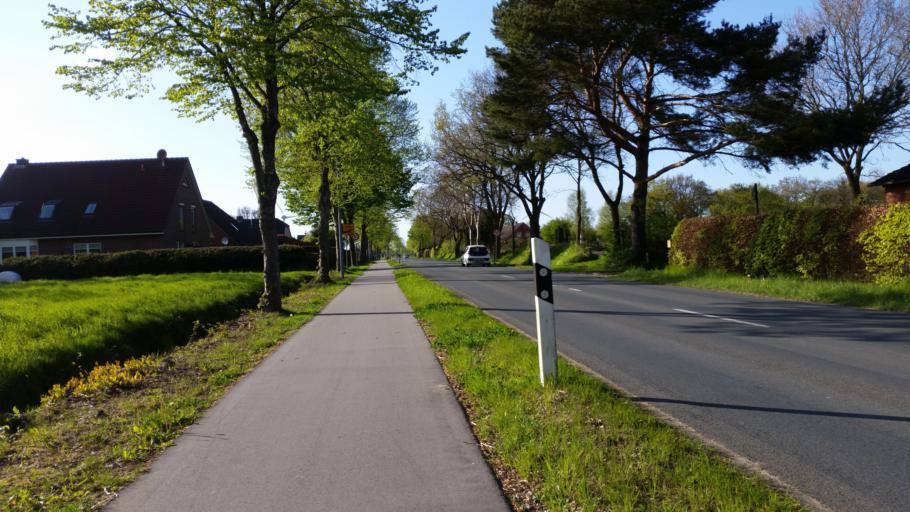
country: DE
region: Lower Saxony
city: Aurich
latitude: 53.4811
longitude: 7.4500
